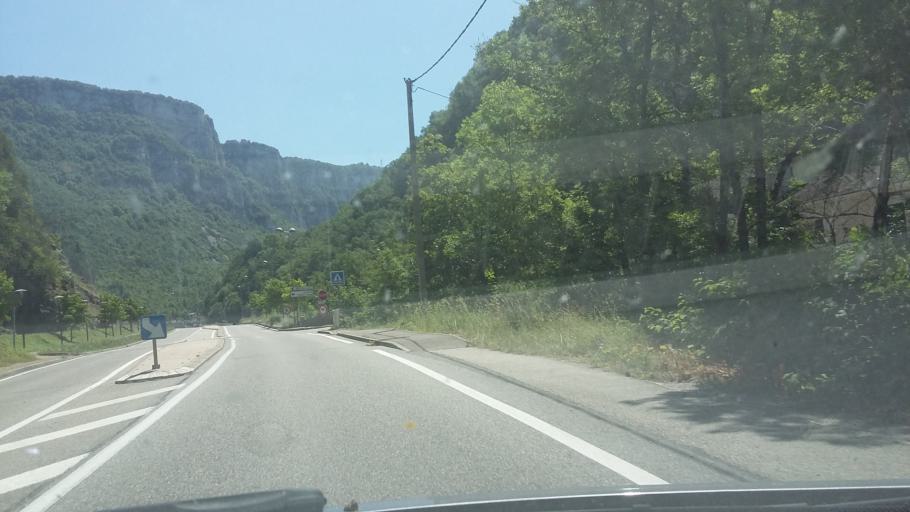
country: FR
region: Rhone-Alpes
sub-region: Departement de l'Ain
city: Tenay
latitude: 45.9232
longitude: 5.5012
